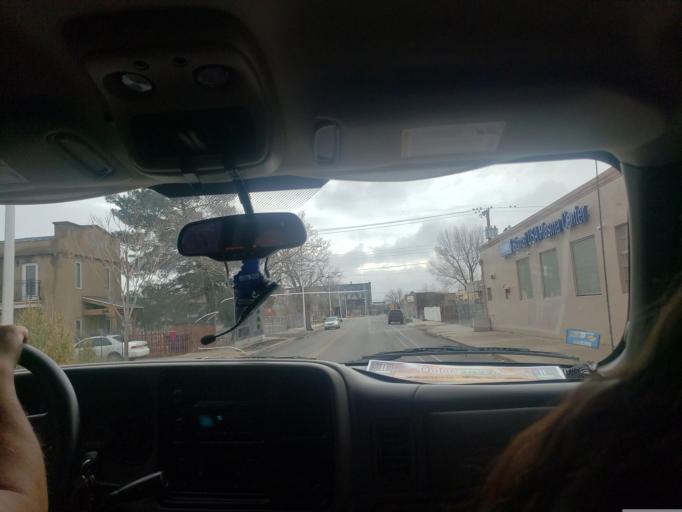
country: US
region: New Mexico
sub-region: Bernalillo County
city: Albuquerque
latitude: 35.0784
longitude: -106.6504
